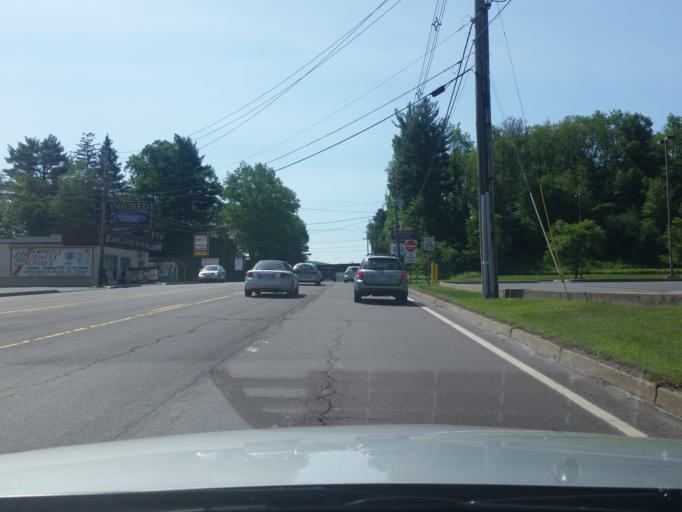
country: US
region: Pennsylvania
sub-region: Luzerne County
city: Shavertown
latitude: 41.3274
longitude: -75.9467
